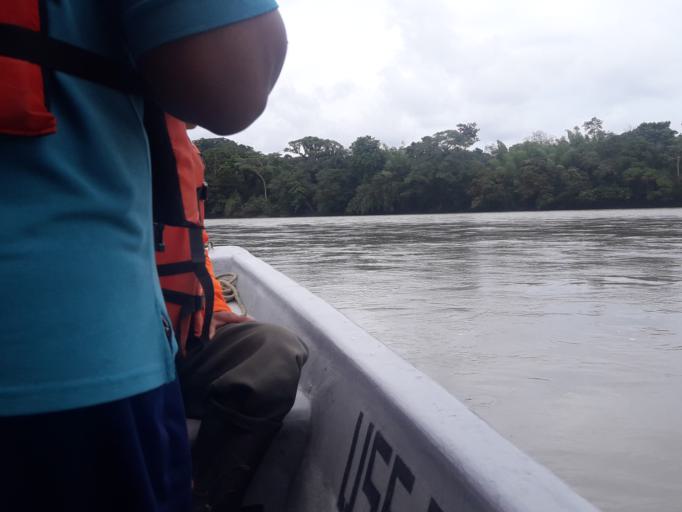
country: EC
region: Orellana
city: Boca Suno
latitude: -0.8789
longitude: -77.2854
